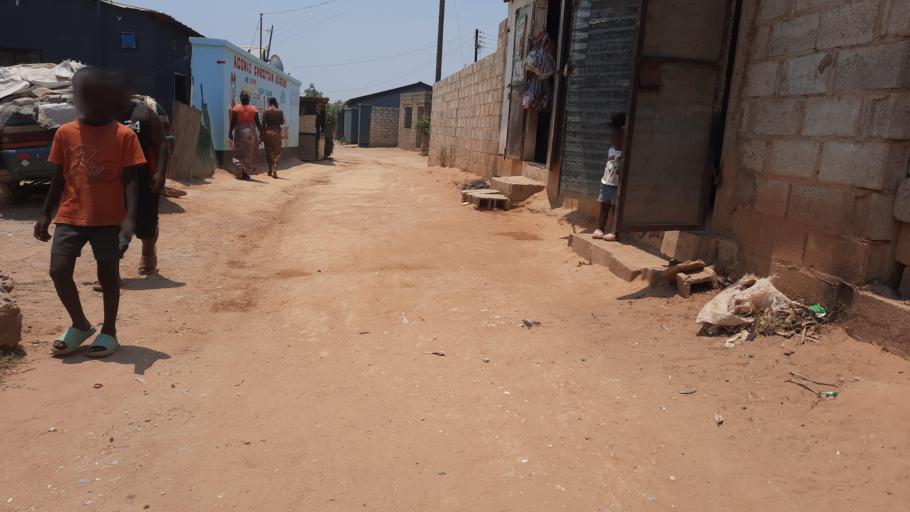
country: ZM
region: Lusaka
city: Lusaka
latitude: -15.4042
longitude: 28.3820
